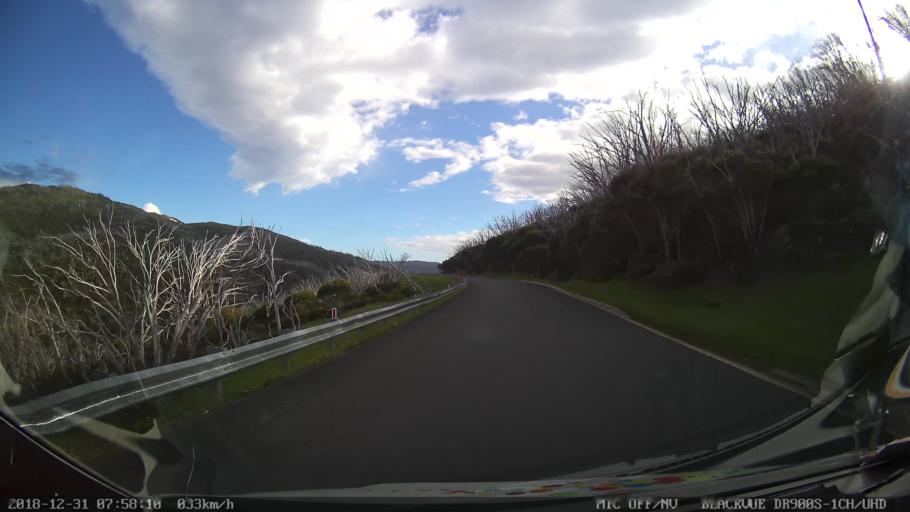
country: AU
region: New South Wales
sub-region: Snowy River
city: Jindabyne
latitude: -36.3762
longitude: 148.3782
